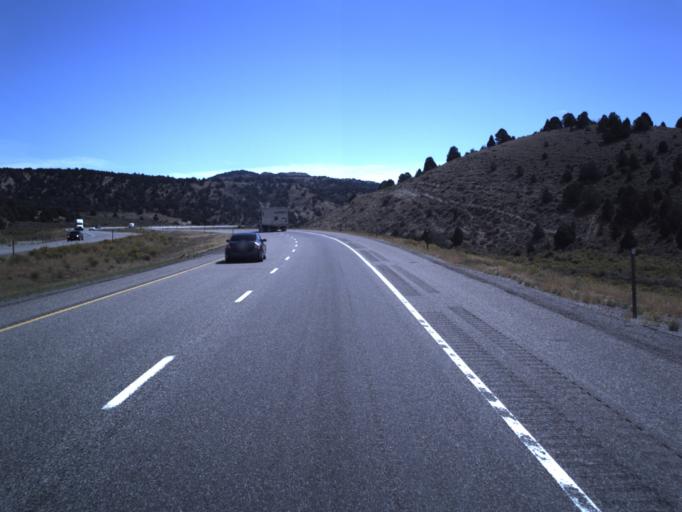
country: US
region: Utah
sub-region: Sevier County
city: Salina
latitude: 38.8030
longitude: -111.5231
